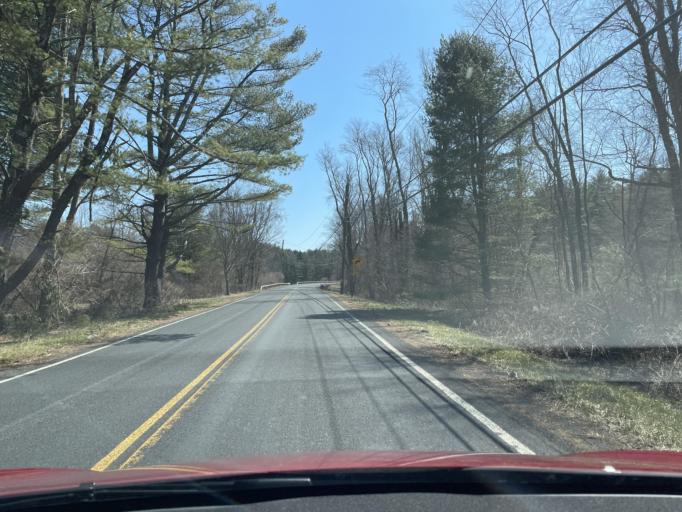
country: US
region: New York
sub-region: Ulster County
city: Shokan
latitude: 42.0242
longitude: -74.1943
